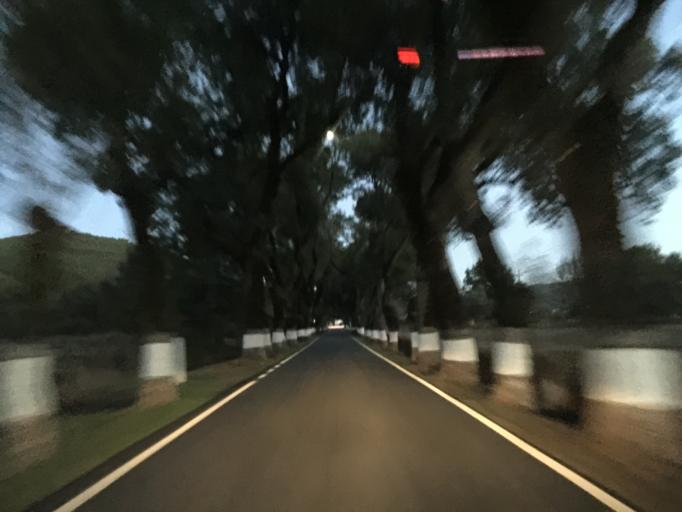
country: PT
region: Portalegre
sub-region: Marvao
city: Marvao
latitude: 39.3807
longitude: -7.3918
